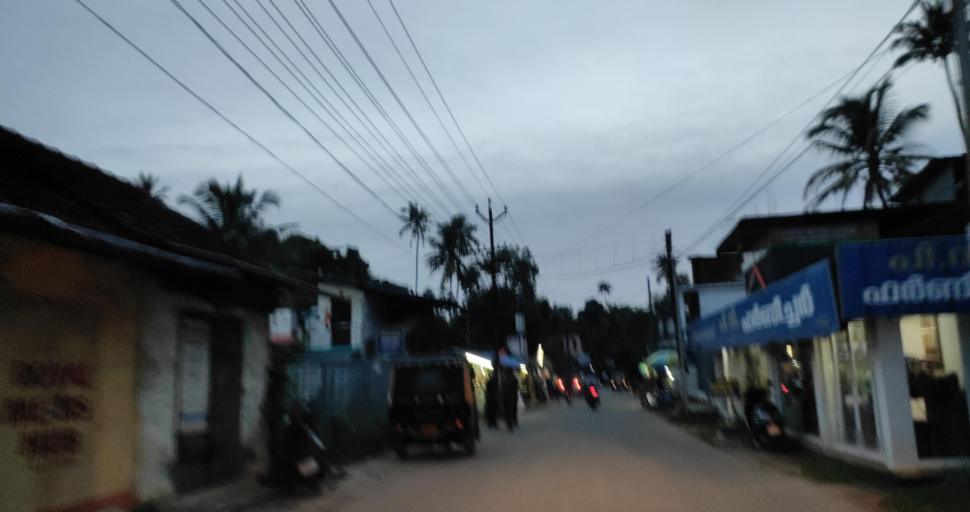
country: IN
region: Kerala
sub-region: Alappuzha
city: Vayalar
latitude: 9.7062
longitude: 76.3022
